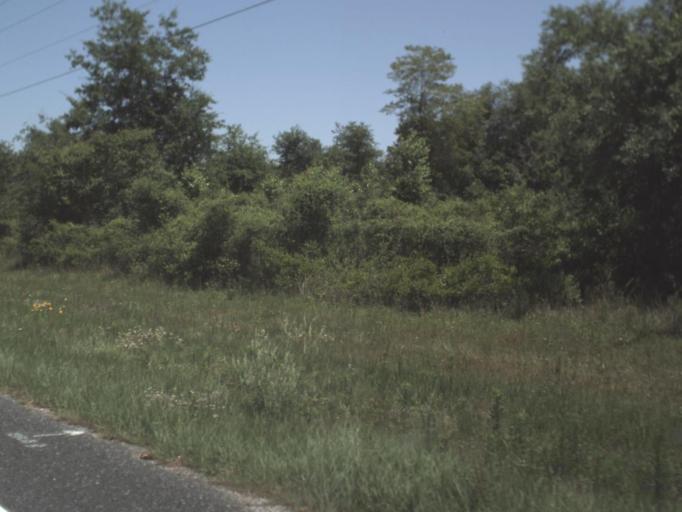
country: US
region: Florida
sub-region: Baker County
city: Macclenny
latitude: 30.2326
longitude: -82.3215
